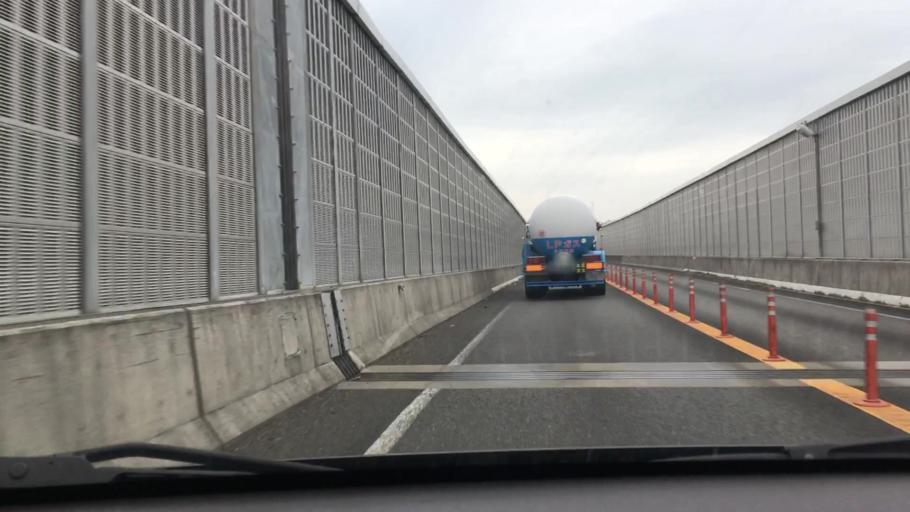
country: JP
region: Mie
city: Kameyama
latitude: 34.8582
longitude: 136.4190
